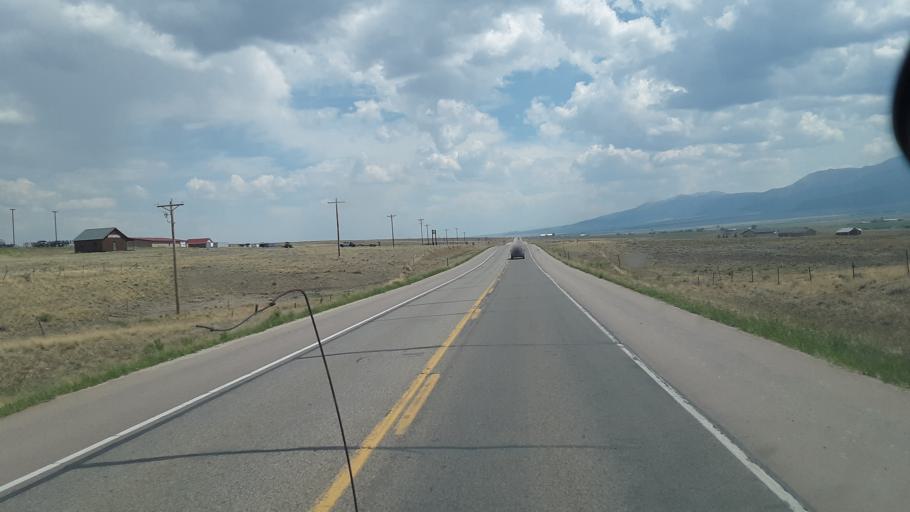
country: US
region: Colorado
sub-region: Custer County
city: Westcliffe
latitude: 38.1279
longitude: -105.4632
